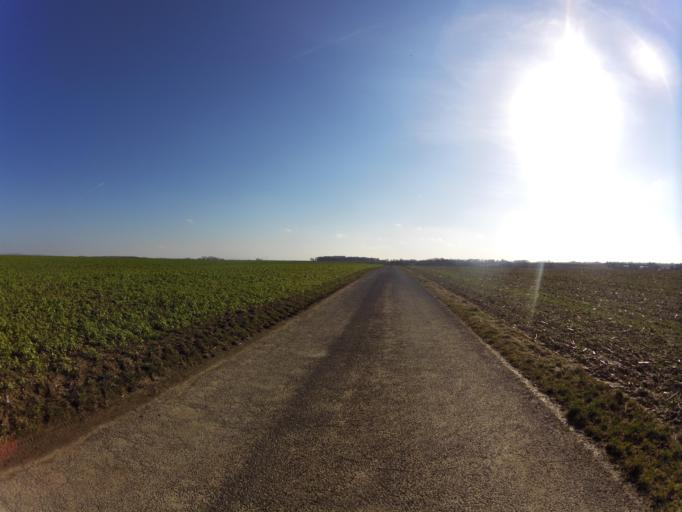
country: DE
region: Bavaria
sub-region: Regierungsbezirk Unterfranken
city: Giebelstadt
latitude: 49.6769
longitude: 9.9741
